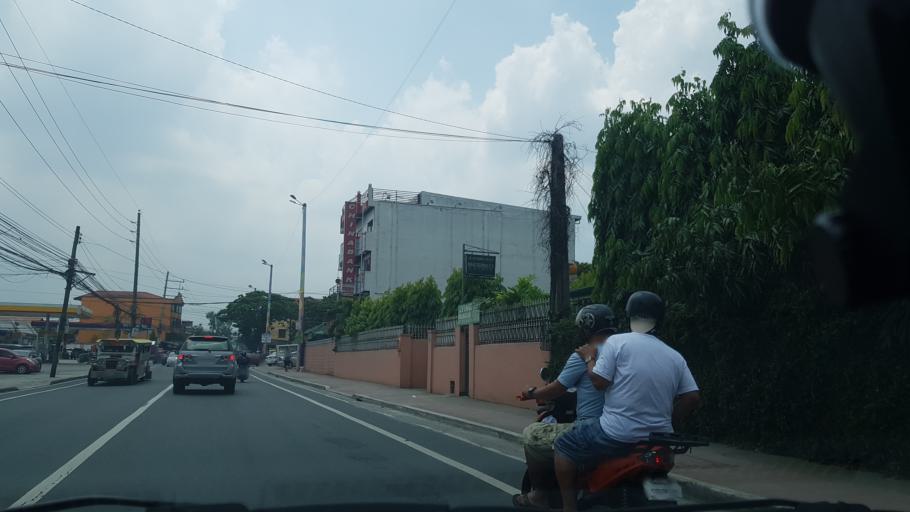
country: PH
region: Calabarzon
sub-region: Province of Rizal
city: San Mateo
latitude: 14.6640
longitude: 121.1065
